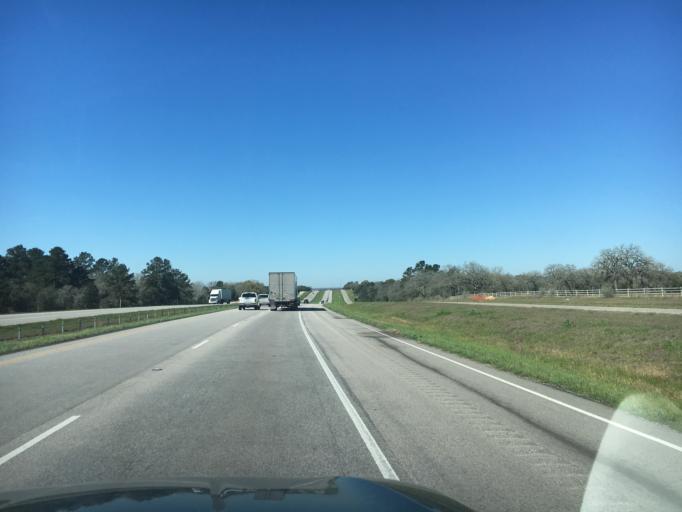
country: US
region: Texas
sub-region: Colorado County
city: Columbus
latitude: 29.7192
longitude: -96.4414
